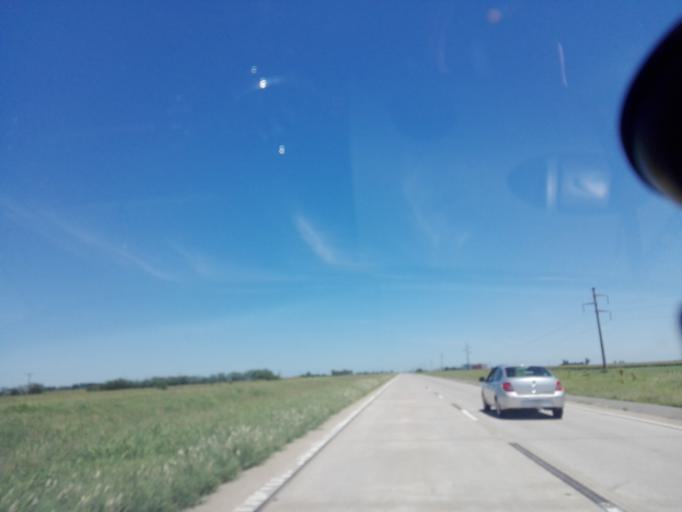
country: AR
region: Santa Fe
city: Canada de Gomez
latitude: -32.8630
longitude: -61.2940
